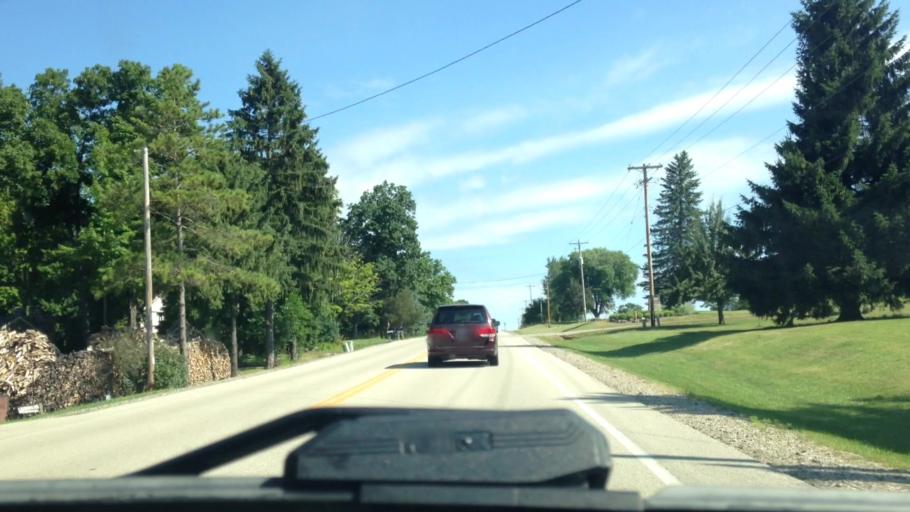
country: US
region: Wisconsin
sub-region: Washington County
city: West Bend
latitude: 43.4034
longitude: -88.2411
